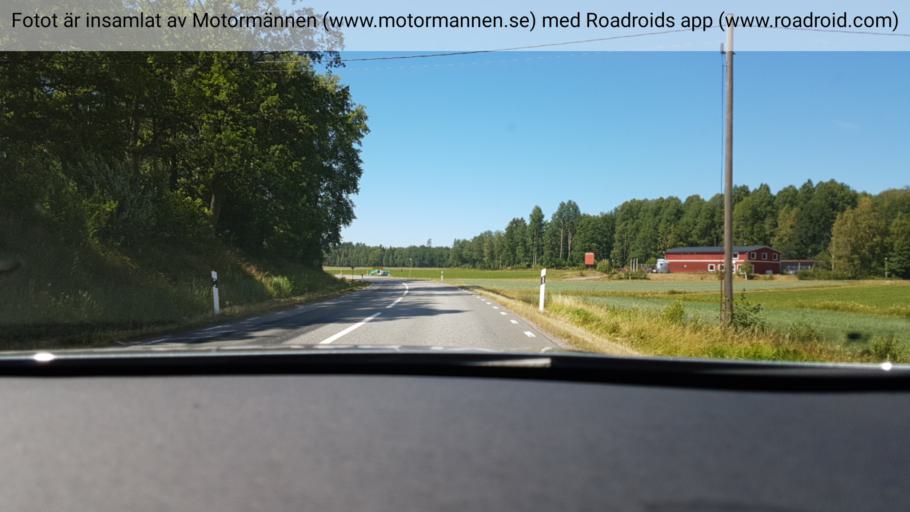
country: SE
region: Joenkoeping
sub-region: Jonkopings Kommun
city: Asa
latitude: 58.0182
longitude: 14.7042
